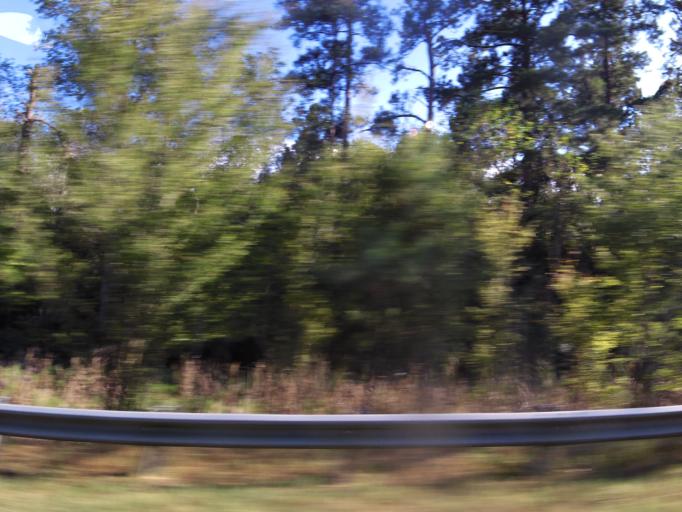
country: US
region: Georgia
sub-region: Brooks County
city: Quitman
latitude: 30.7898
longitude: -83.4880
